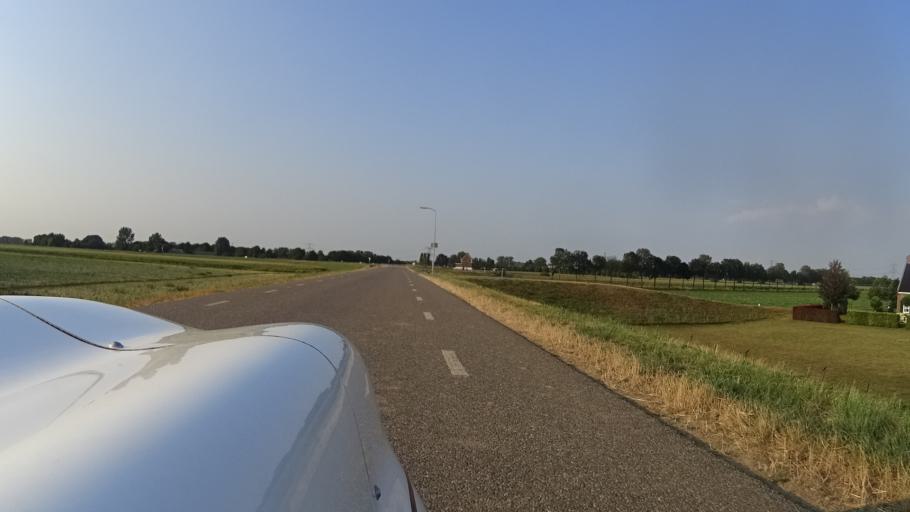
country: NL
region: Gelderland
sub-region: Gemeente Wijchen
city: Bergharen
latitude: 51.8082
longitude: 5.6581
